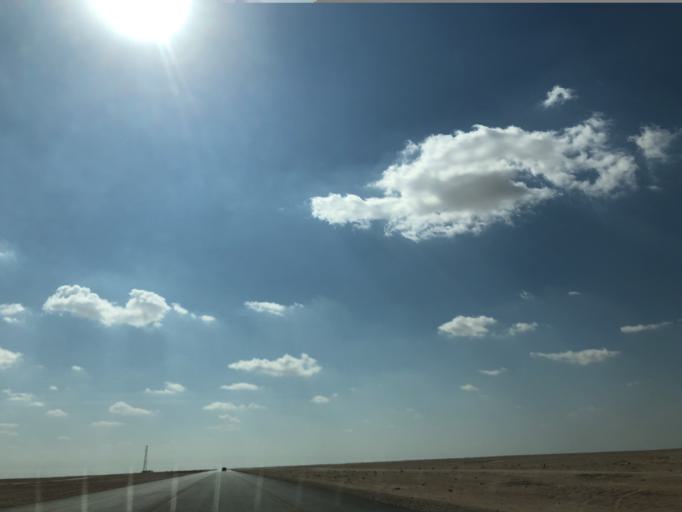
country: OM
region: Al Wusta
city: Hayma'
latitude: 20.2506
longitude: 56.5790
